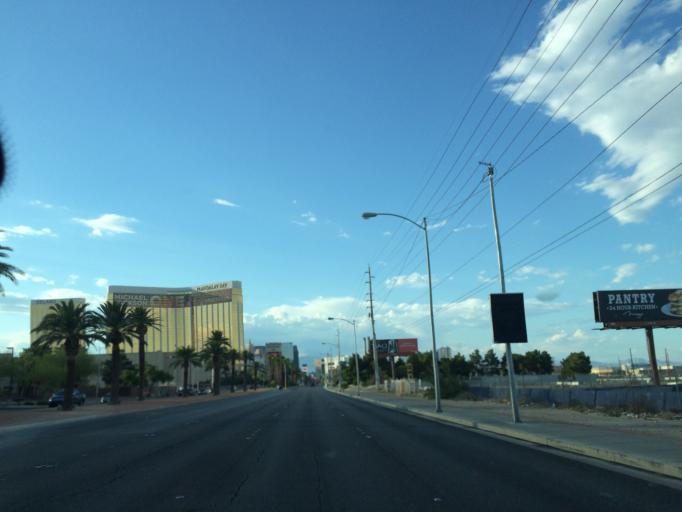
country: US
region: Nevada
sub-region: Clark County
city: Paradise
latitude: 36.0839
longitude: -115.1726
